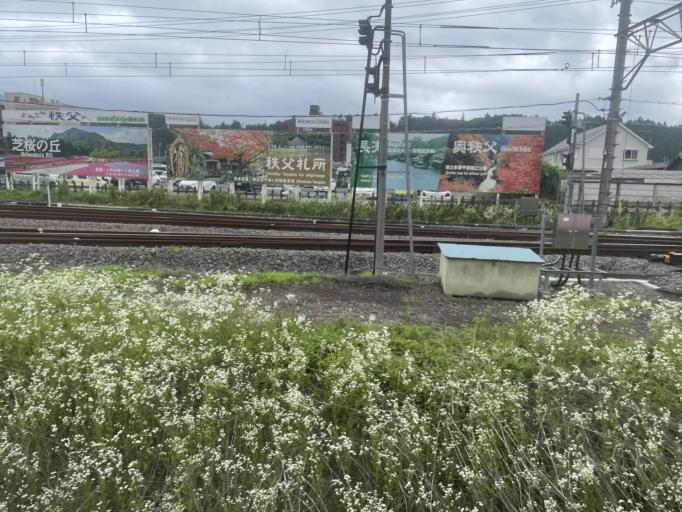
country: JP
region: Saitama
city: Chichibu
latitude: 35.9888
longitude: 139.0825
